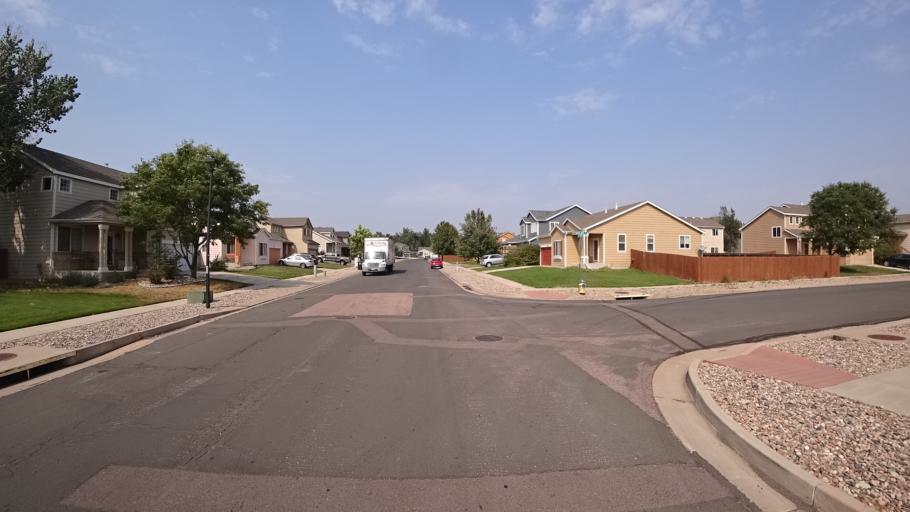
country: US
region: Colorado
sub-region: El Paso County
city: Cimarron Hills
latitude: 38.8269
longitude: -104.7440
